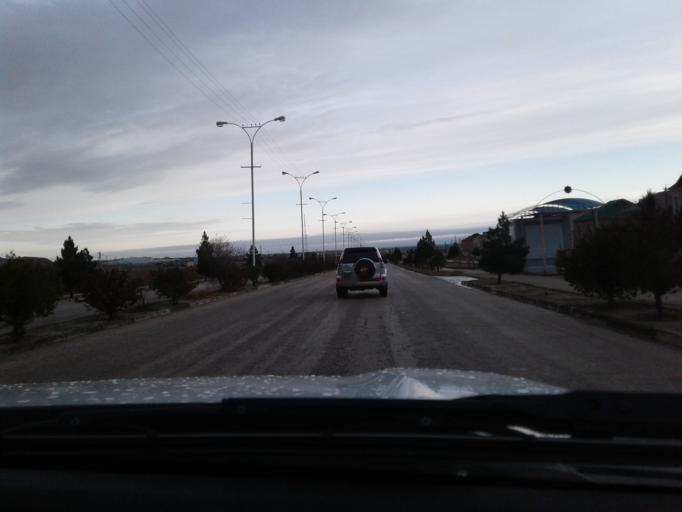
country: TM
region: Balkan
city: Balkanabat
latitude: 39.5371
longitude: 54.3510
